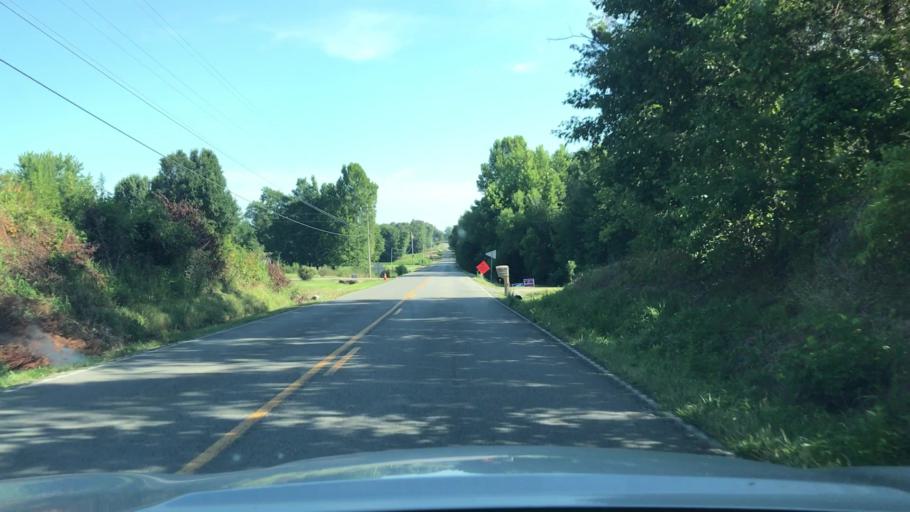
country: US
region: Kentucky
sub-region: Muhlenberg County
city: Greenville
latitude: 37.1494
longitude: -87.1414
